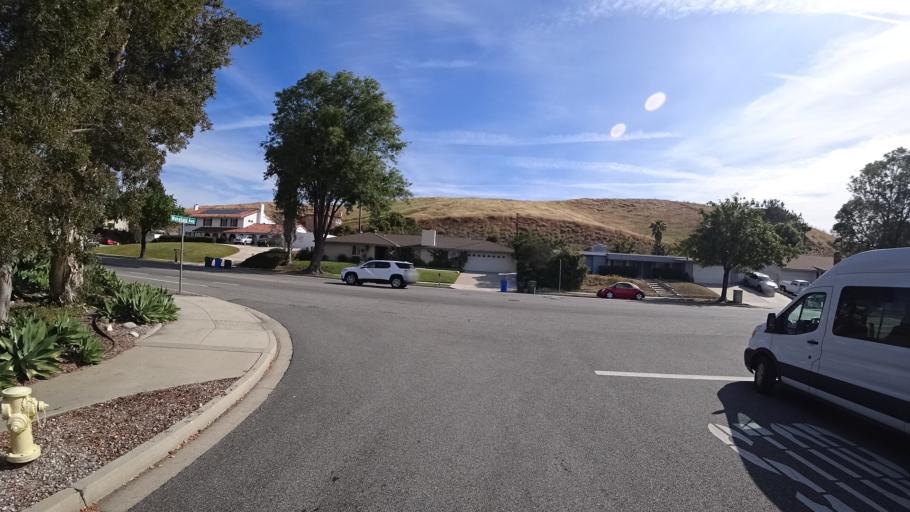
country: US
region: California
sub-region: Ventura County
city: Thousand Oaks
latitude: 34.2009
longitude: -118.8745
